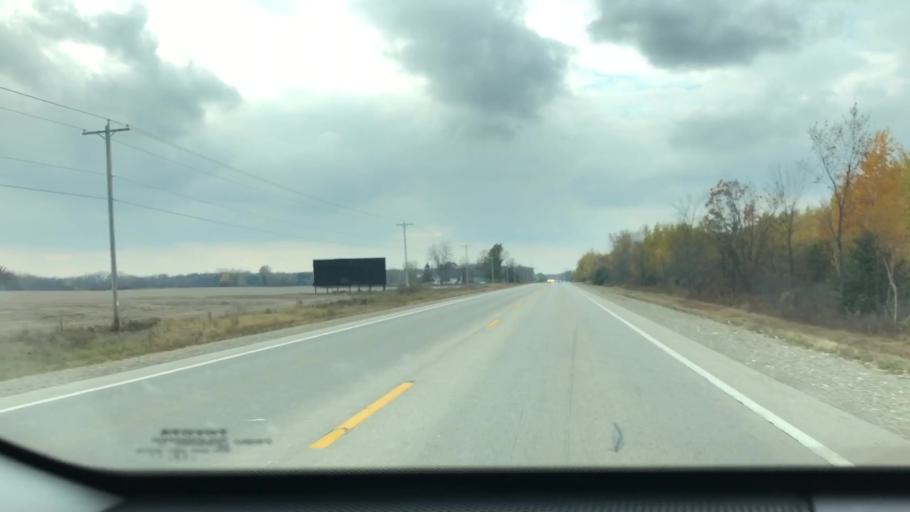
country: US
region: Wisconsin
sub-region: Brown County
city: Oneida
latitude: 44.5021
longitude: -88.2178
